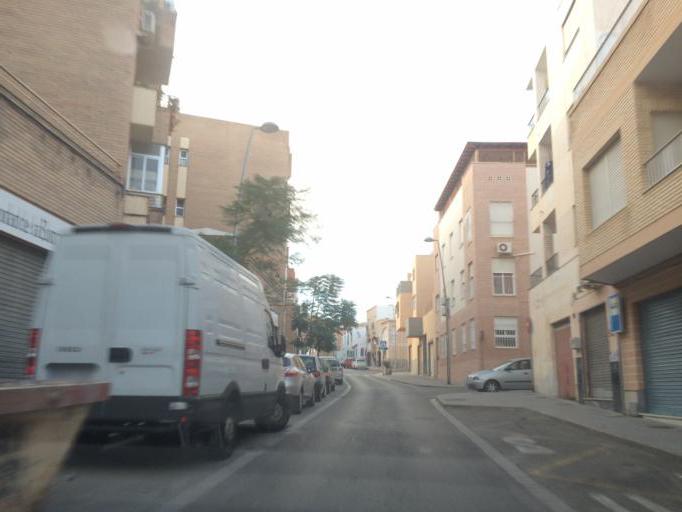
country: ES
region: Andalusia
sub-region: Provincia de Almeria
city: Almeria
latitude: 36.8485
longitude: -2.4701
